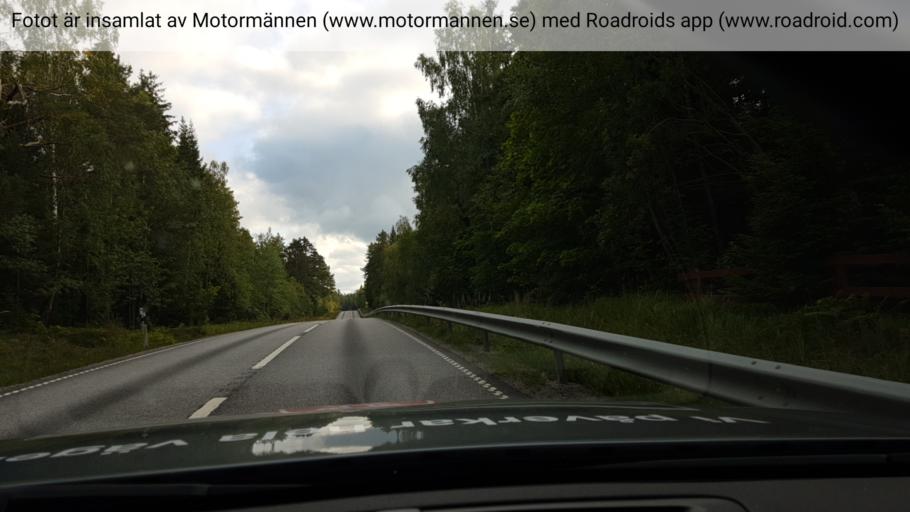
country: SE
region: Stockholm
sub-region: Norrtalje Kommun
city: Hallstavik
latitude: 60.0027
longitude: 18.5850
